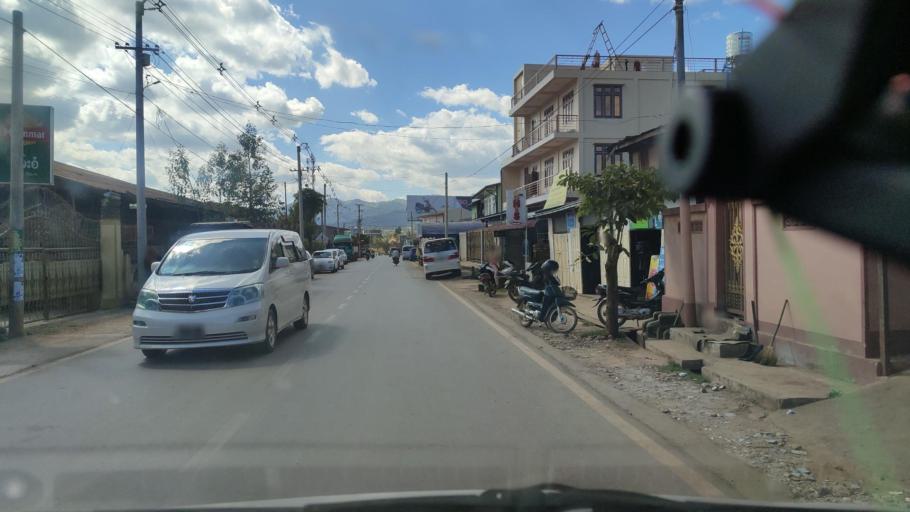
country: MM
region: Shan
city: Taunggyi
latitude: 20.9910
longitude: 97.5304
